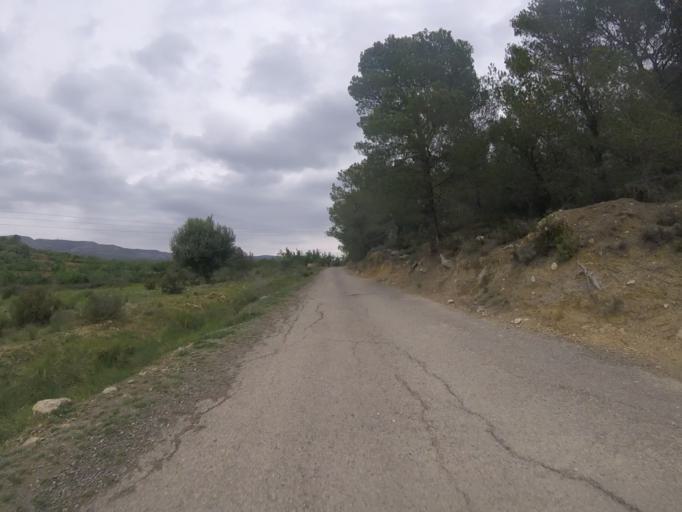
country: ES
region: Valencia
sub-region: Provincia de Castello
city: Sarratella
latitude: 40.2742
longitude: 0.0714
